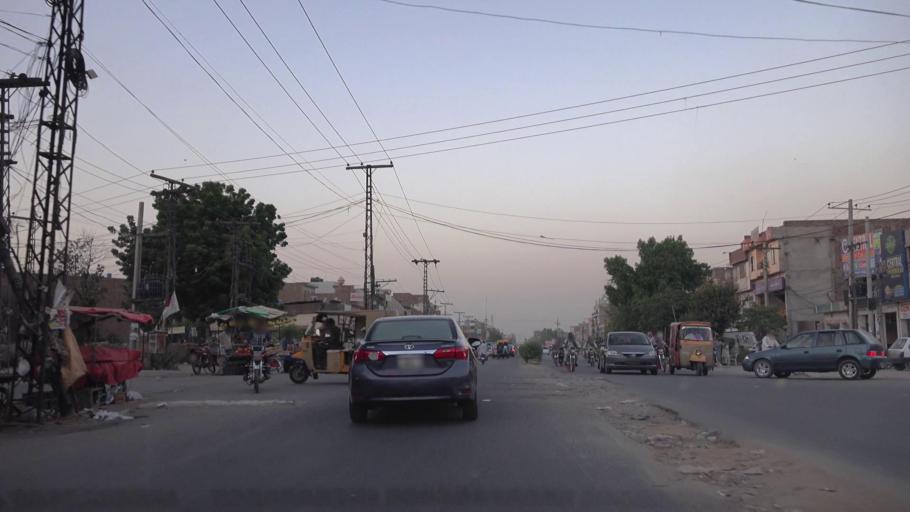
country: PK
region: Punjab
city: Faisalabad
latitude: 31.4494
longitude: 73.0976
